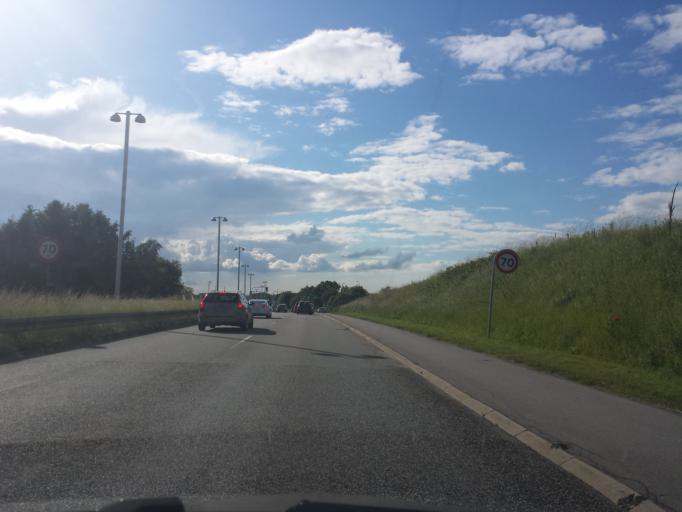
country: DK
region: Capital Region
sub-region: Ballerup Kommune
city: Malov
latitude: 55.7443
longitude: 12.3307
